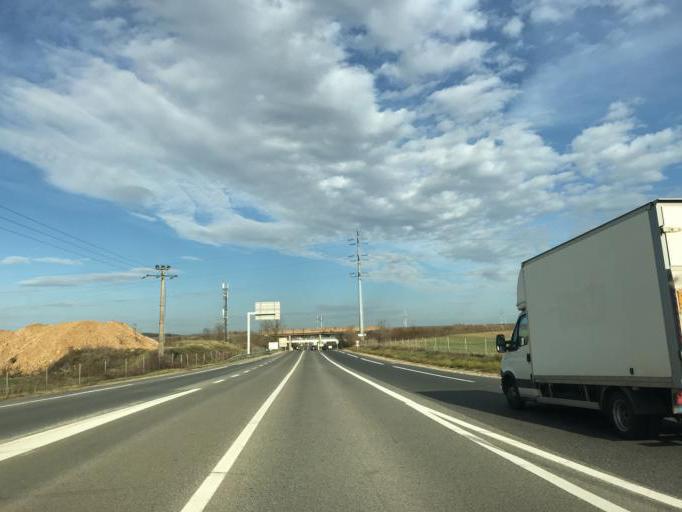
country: FR
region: Rhone-Alpes
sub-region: Departement du Rhone
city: Cailloux-sur-Fontaines
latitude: 45.8569
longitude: 4.9103
